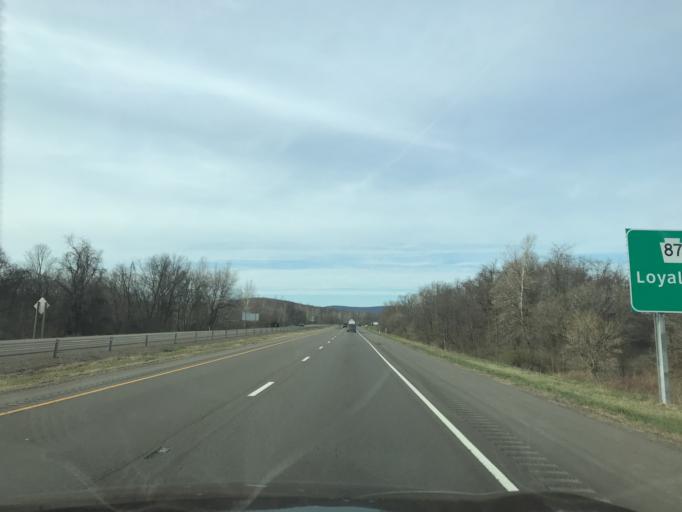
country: US
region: Pennsylvania
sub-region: Lycoming County
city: Montoursville
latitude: 41.2548
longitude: -76.9308
